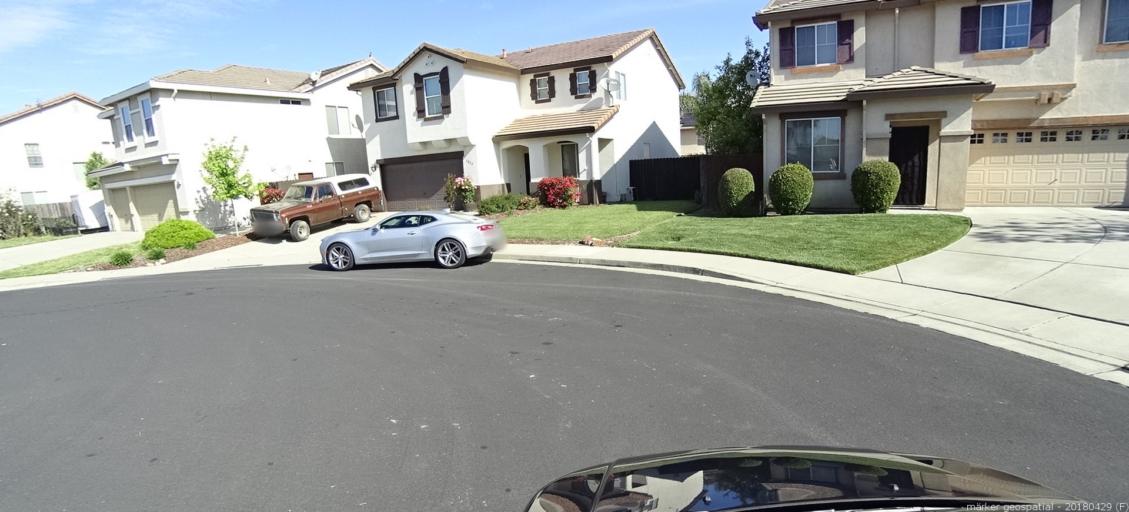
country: US
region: California
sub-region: Yolo County
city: West Sacramento
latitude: 38.5417
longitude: -121.5594
